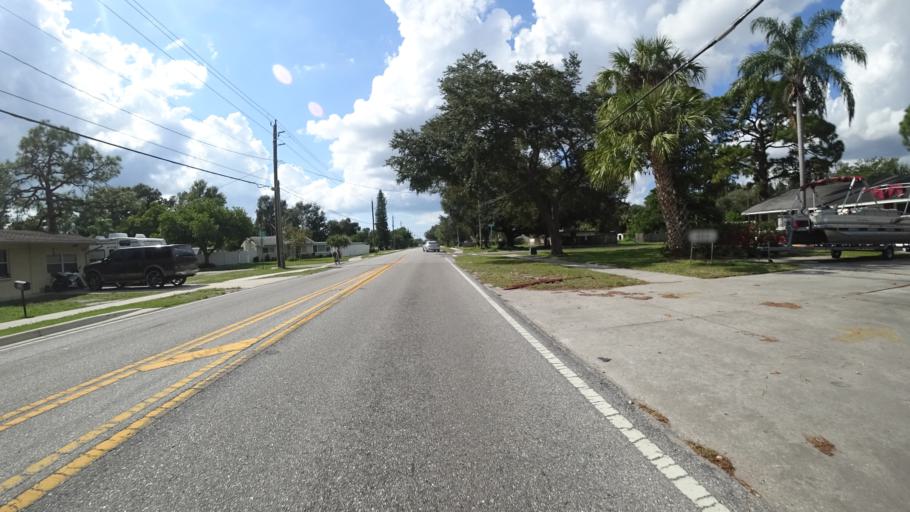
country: US
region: Florida
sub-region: Manatee County
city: Bayshore Gardens
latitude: 27.4404
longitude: -82.5779
